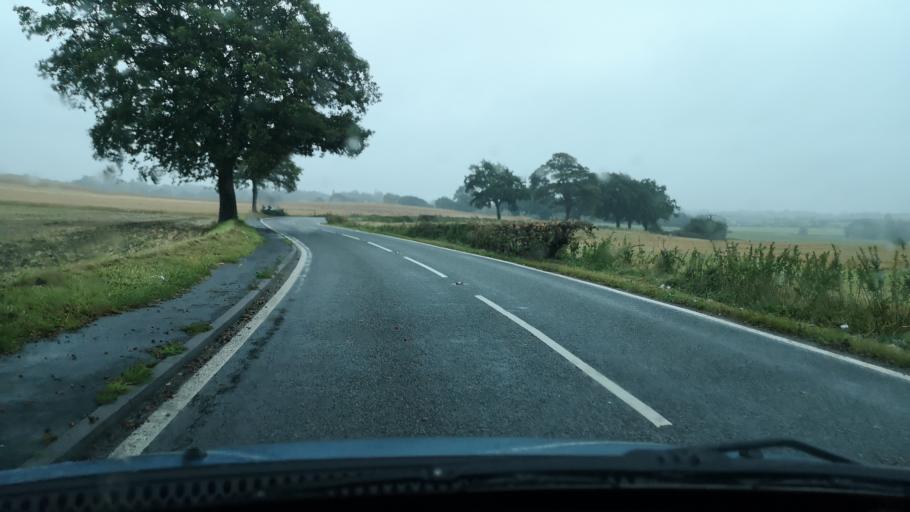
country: GB
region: England
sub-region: City and Borough of Wakefield
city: Featherstone
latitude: 53.6646
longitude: -1.3492
